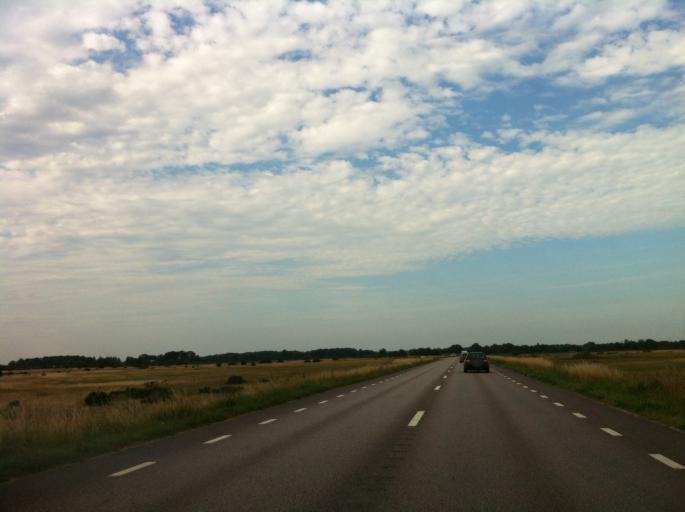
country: SE
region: Kalmar
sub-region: Borgholms Kommun
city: Borgholm
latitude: 56.9799
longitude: 16.8084
